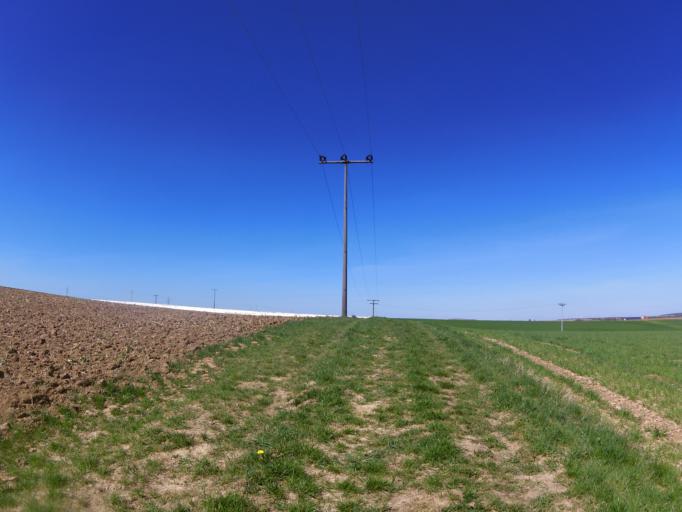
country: DE
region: Bavaria
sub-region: Regierungsbezirk Unterfranken
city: Biebelried
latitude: 49.7988
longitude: 10.0996
